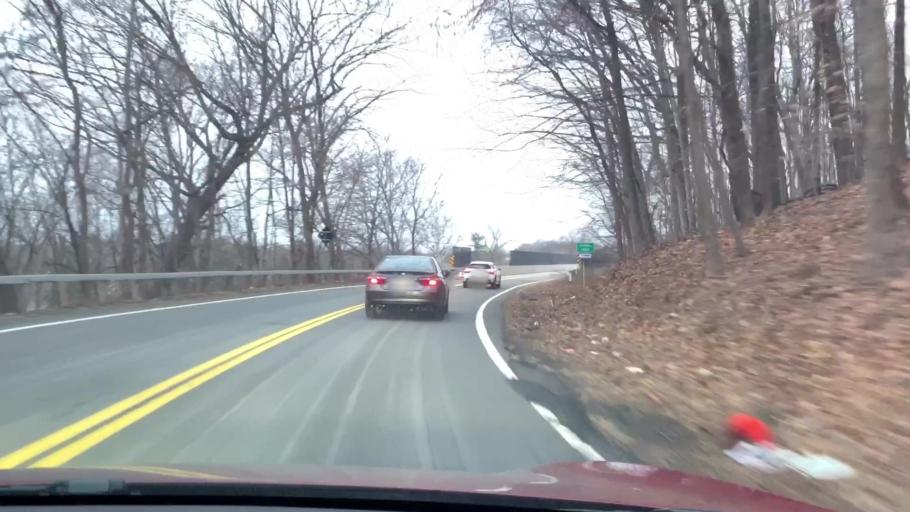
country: US
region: New York
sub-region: Rockland County
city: Sparkill
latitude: 41.0287
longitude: -73.9236
